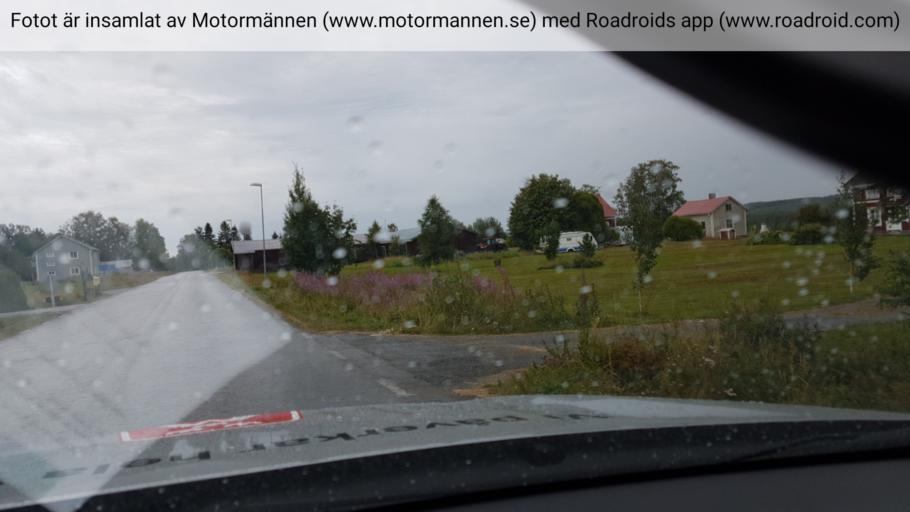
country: SE
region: Norrbotten
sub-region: Bodens Kommun
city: Boden
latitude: 65.9022
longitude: 21.3162
